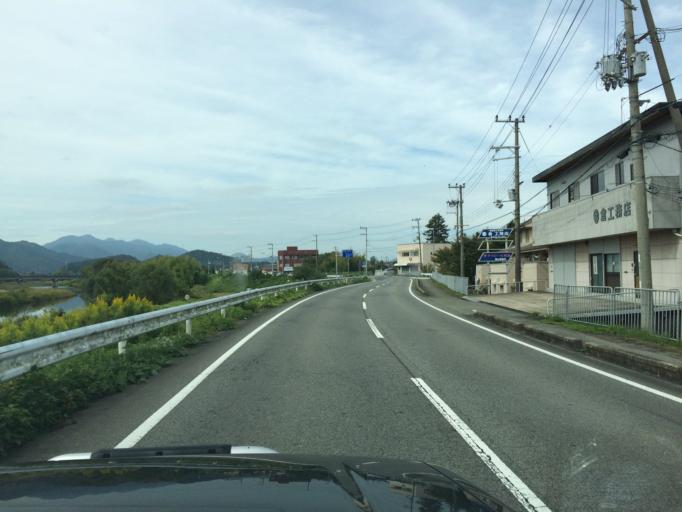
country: JP
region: Hyogo
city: Sasayama
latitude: 35.0706
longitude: 135.2263
